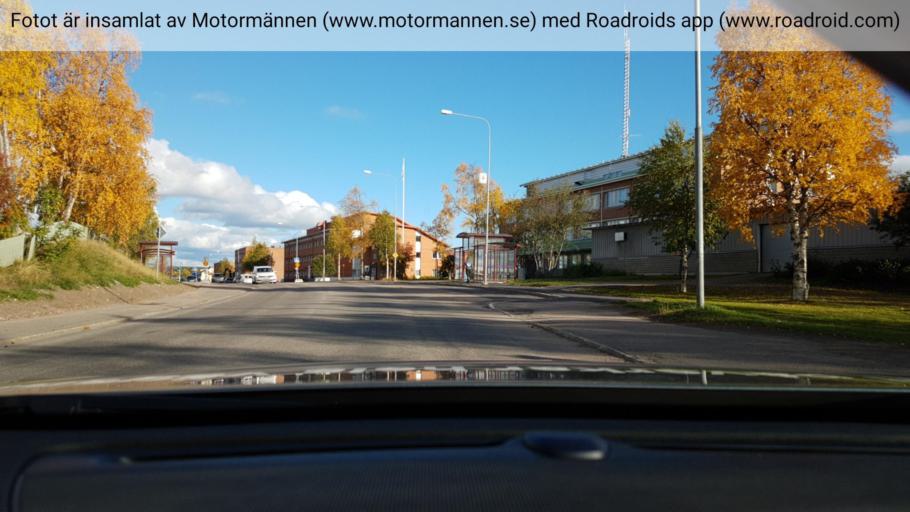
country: SE
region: Norrbotten
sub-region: Gallivare Kommun
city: Gaellivare
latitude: 67.1328
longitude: 20.6606
